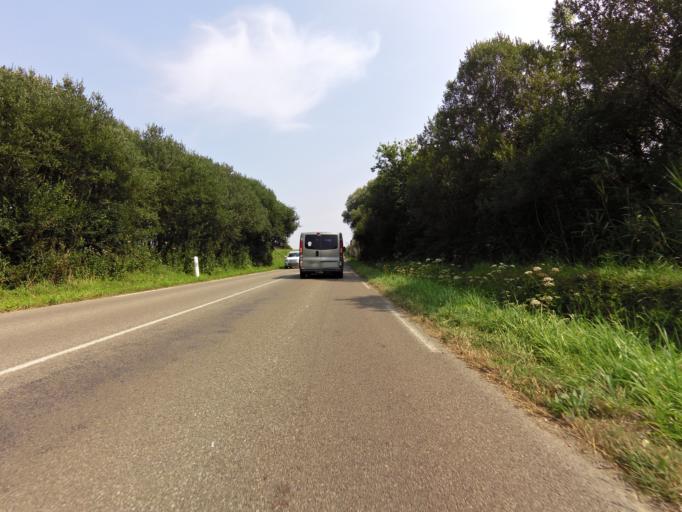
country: FR
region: Brittany
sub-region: Departement du Finistere
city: Esquibien
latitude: 48.0307
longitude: -4.5936
